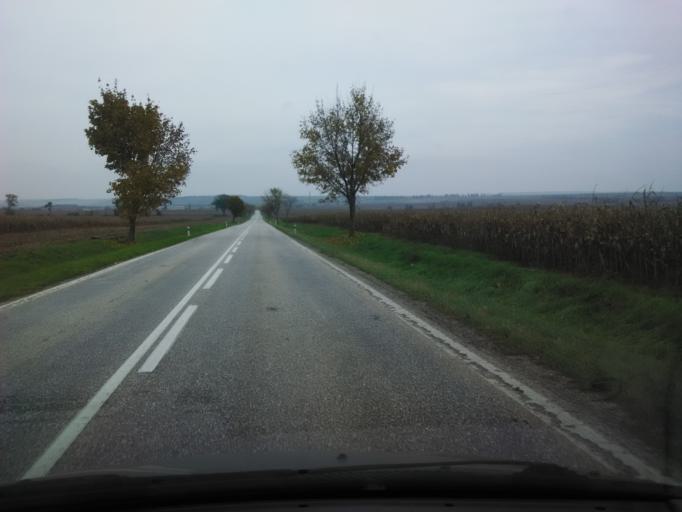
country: SK
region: Nitriansky
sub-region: Okres Nove Zamky
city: Nove Zamky
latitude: 47.9923
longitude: 18.3350
